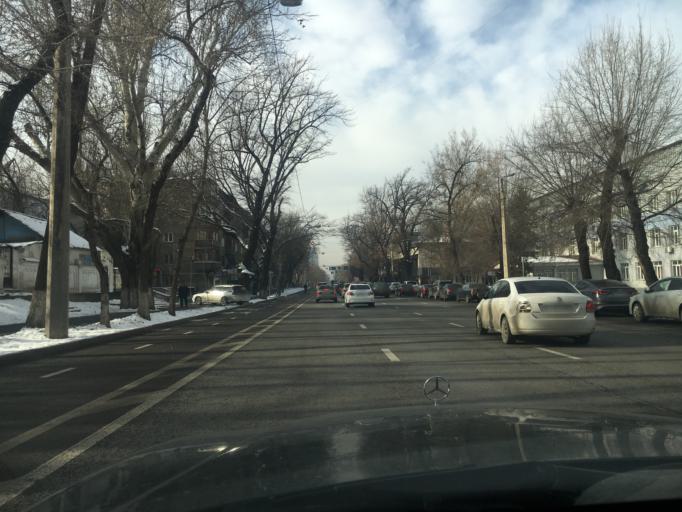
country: KZ
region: Almaty Qalasy
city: Almaty
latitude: 43.2452
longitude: 76.9298
